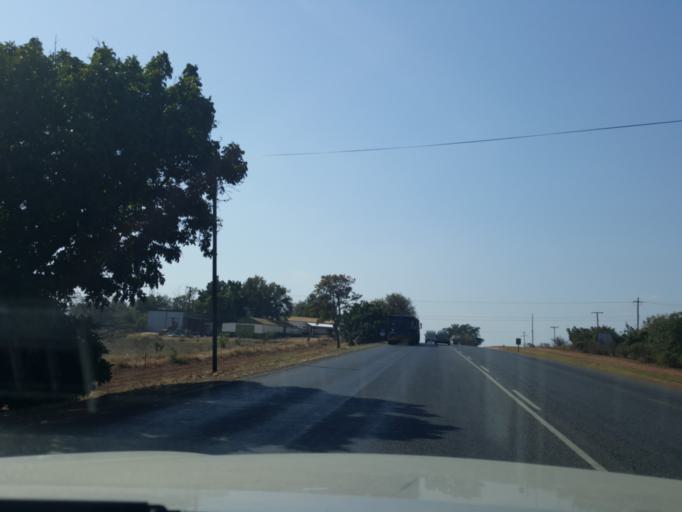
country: SZ
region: Hhohho
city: Ntfonjeni
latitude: -25.4938
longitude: 31.5214
